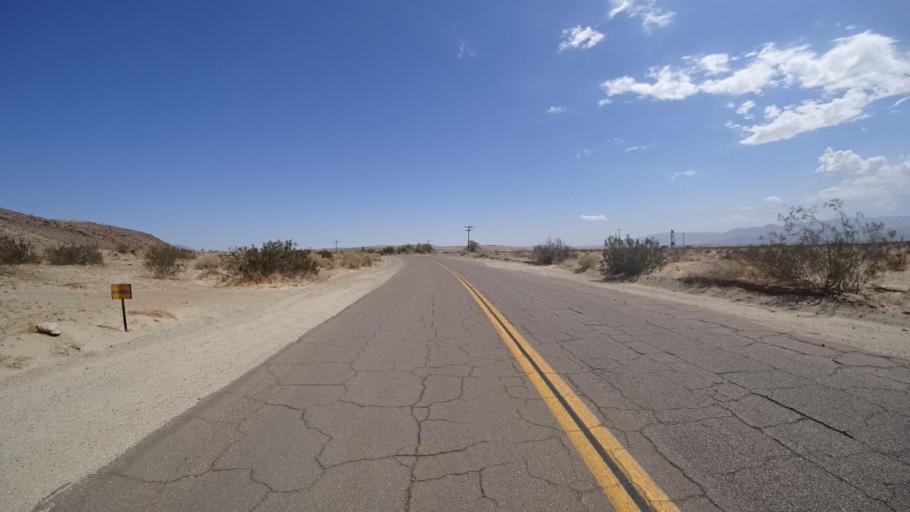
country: US
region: California
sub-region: San Diego County
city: Borrego Springs
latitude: 33.2969
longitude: -116.3094
